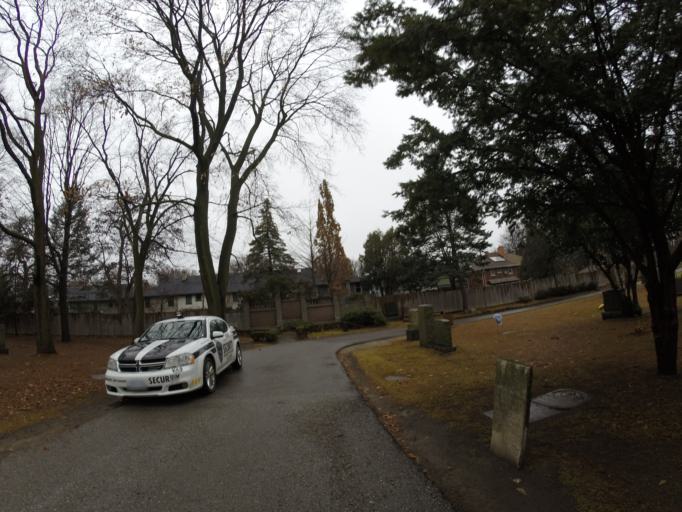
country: CA
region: Ontario
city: Toronto
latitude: 43.6681
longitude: -79.3615
